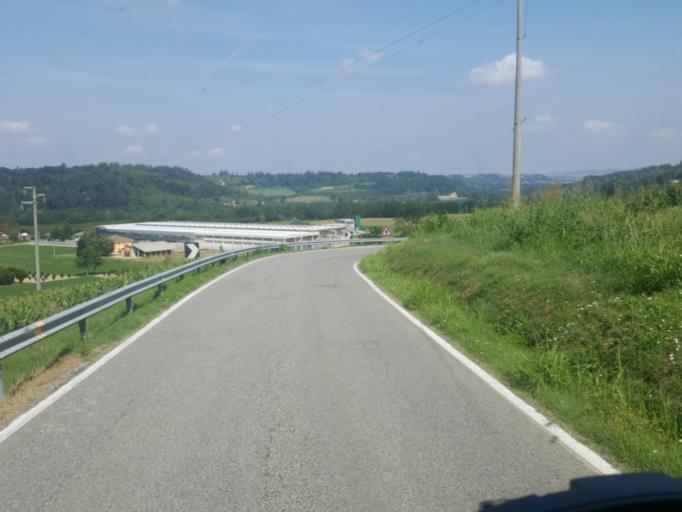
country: IT
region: Piedmont
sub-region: Provincia di Cuneo
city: Narzole
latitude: 44.6051
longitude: 7.8926
